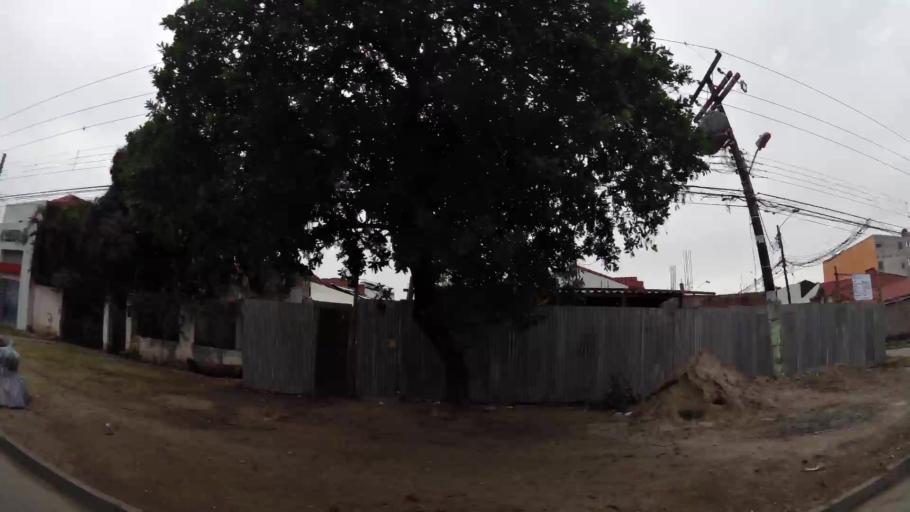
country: BO
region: Santa Cruz
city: Santa Cruz de la Sierra
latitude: -17.7587
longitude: -63.1835
